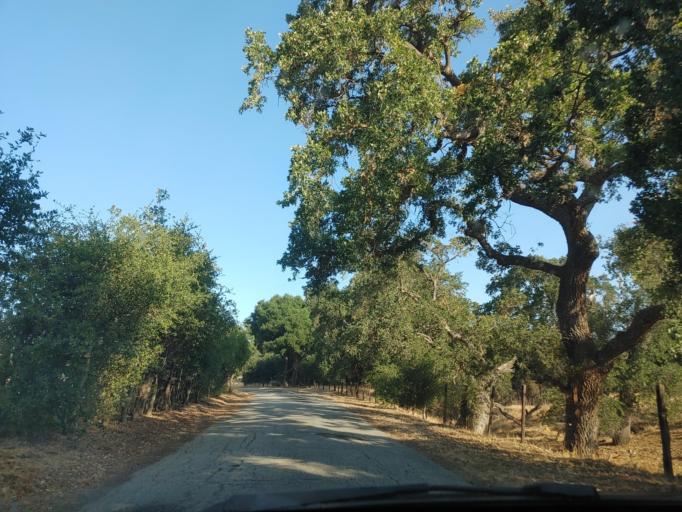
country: US
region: California
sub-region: San Benito County
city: Ridgemark
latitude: 36.7837
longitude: -121.2500
